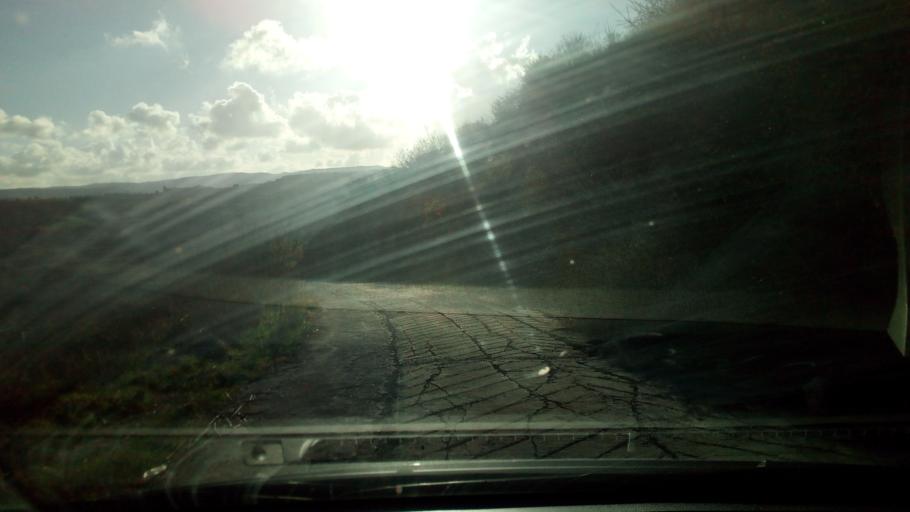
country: CY
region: Pafos
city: Tala
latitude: 34.9111
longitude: 32.5153
